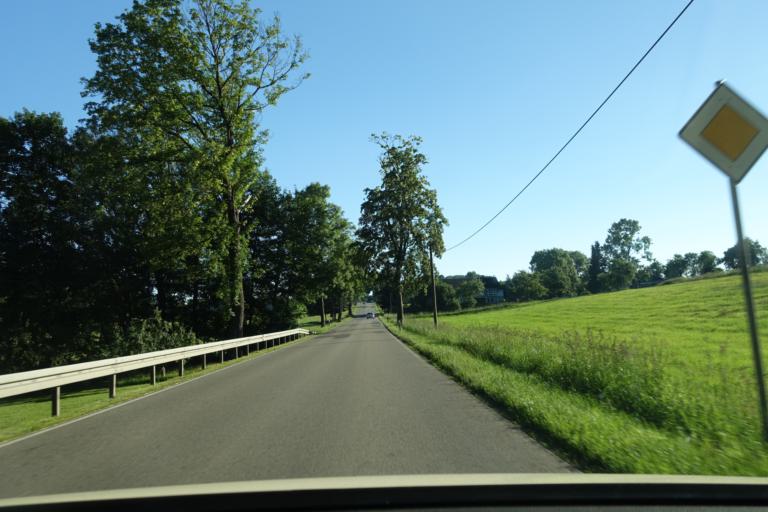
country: DE
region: Saxony
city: Brand-Erbisdorf
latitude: 50.8441
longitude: 13.3009
